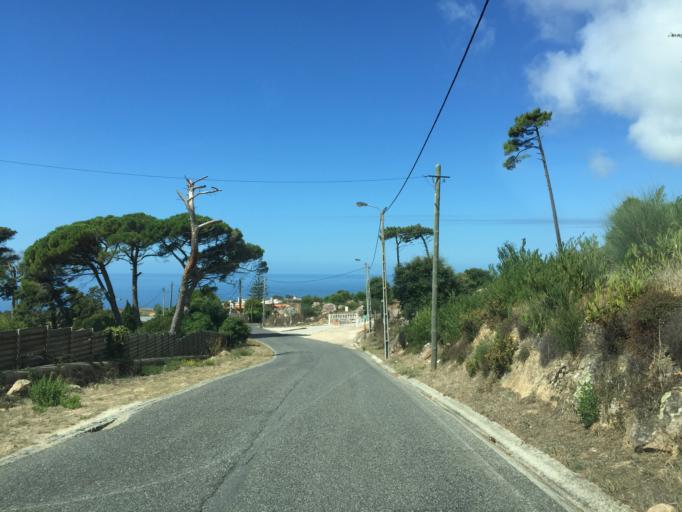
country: PT
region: Lisbon
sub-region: Cascais
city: Alcabideche
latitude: 38.7568
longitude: -9.4430
